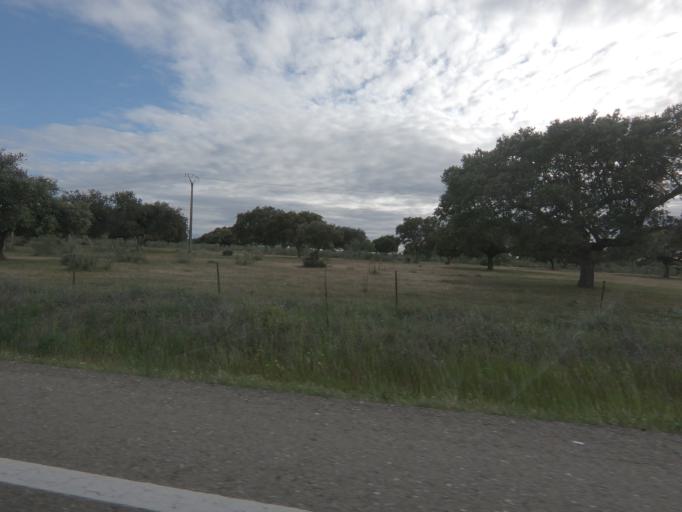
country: ES
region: Extremadura
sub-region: Provincia de Caceres
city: Torrejoncillo
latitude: 39.9190
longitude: -6.4913
